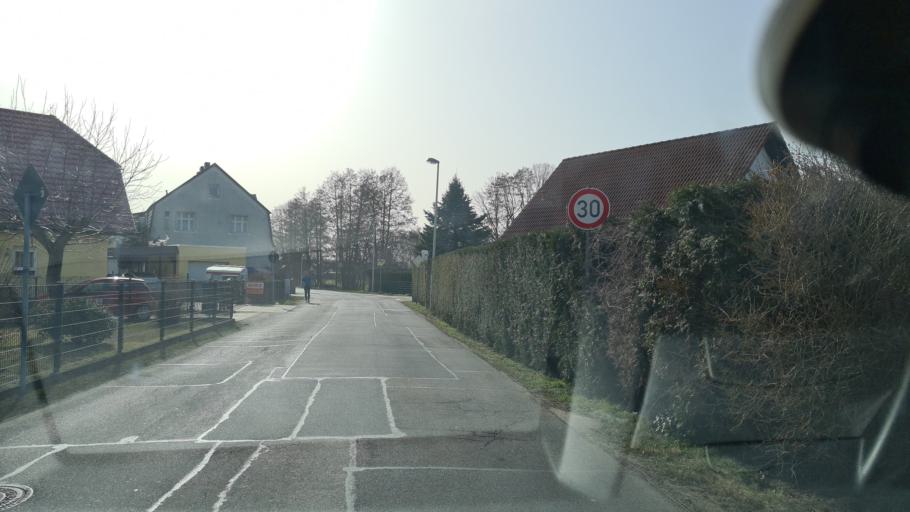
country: DE
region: Brandenburg
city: Cottbus
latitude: 51.7329
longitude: 14.3619
